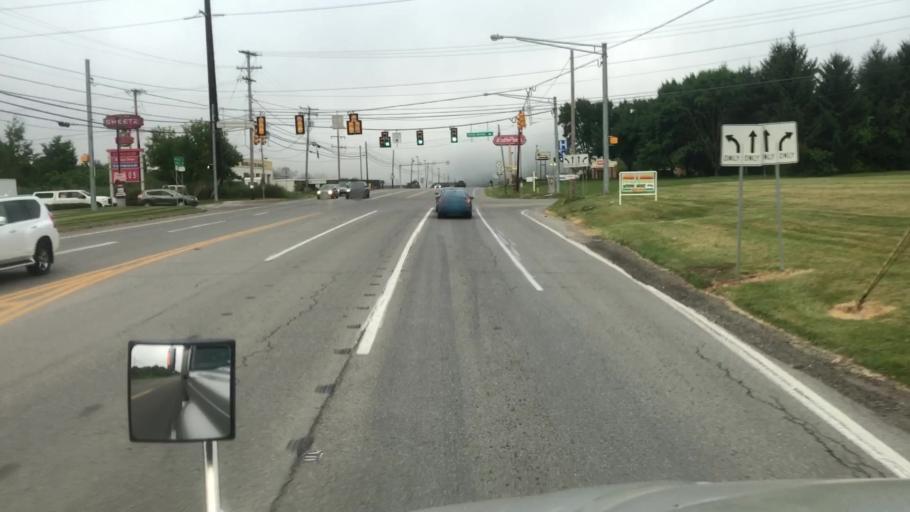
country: US
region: Pennsylvania
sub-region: Venango County
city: Franklin
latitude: 41.4031
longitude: -79.8057
